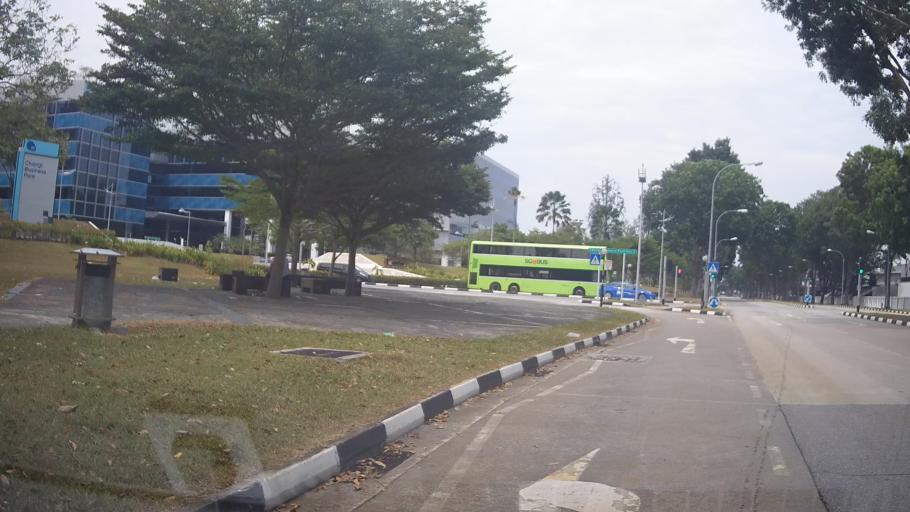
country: SG
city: Singapore
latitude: 1.3330
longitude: 103.9675
